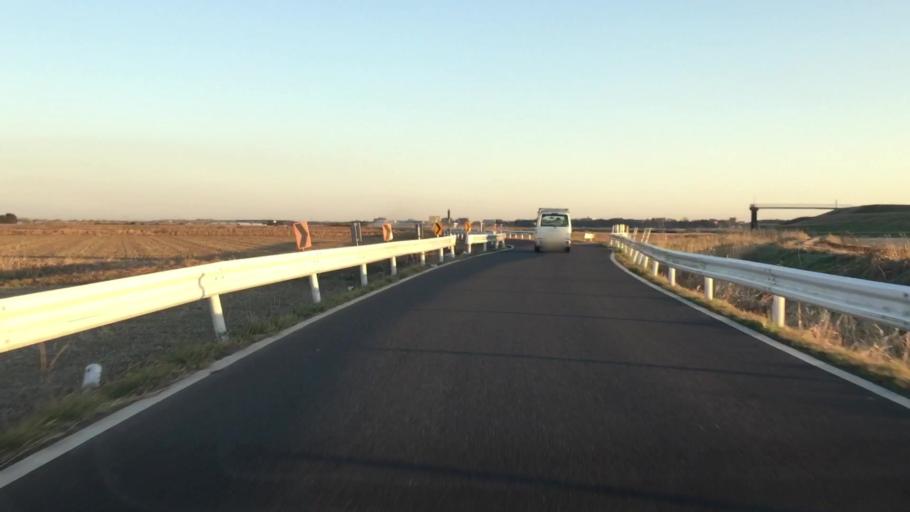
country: JP
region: Chiba
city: Abiko
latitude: 35.8994
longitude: 140.0144
